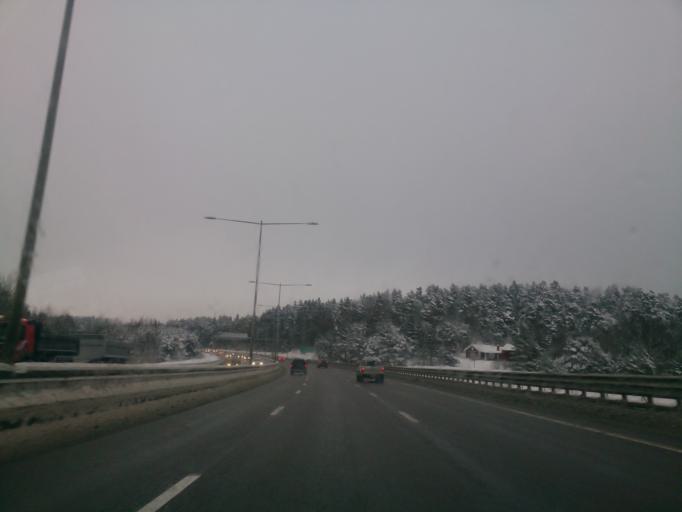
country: SE
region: Stockholm
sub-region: Salems Kommun
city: Ronninge
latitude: 59.2149
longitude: 17.7763
